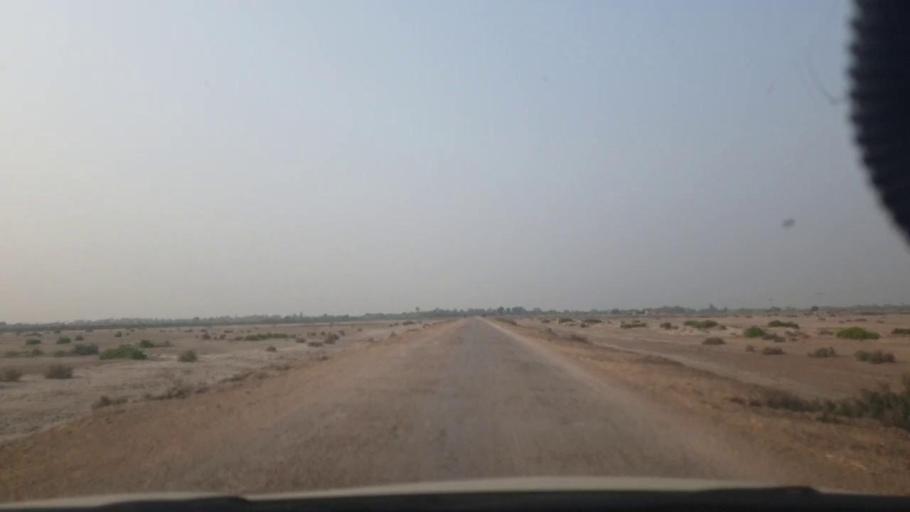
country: PK
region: Sindh
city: Bulri
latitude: 24.8176
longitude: 68.4056
